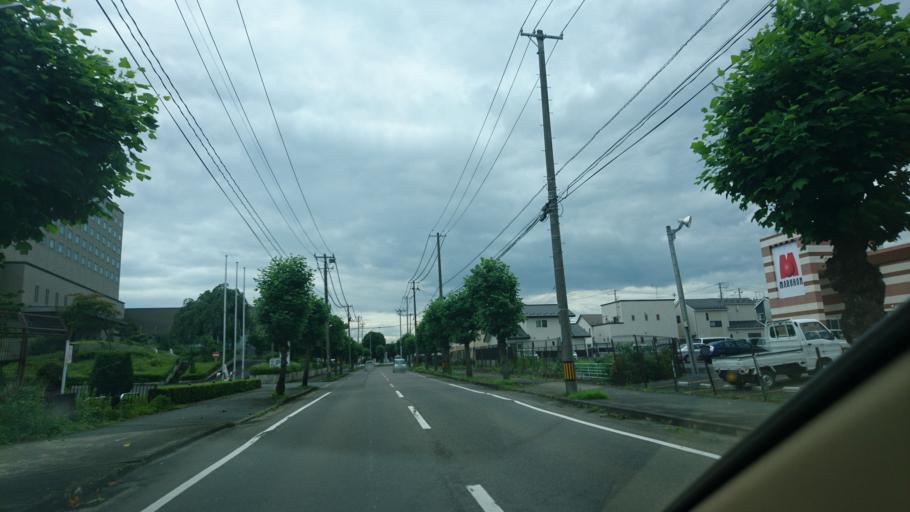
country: JP
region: Iwate
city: Kitakami
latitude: 39.2787
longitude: 141.1229
